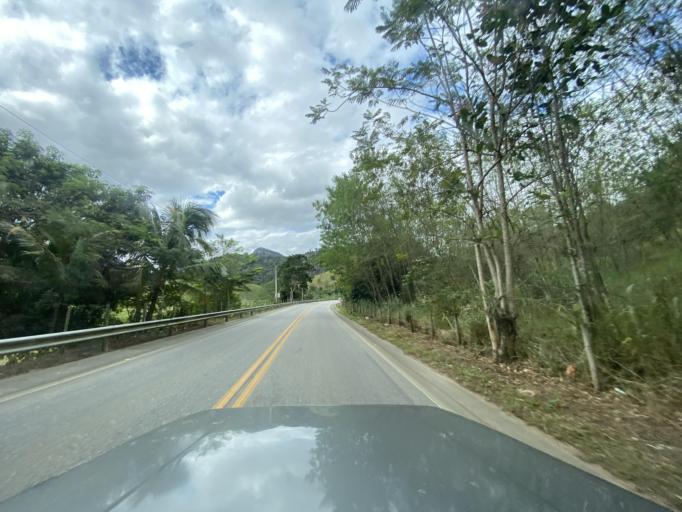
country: BR
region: Espirito Santo
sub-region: Jeronimo Monteiro
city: Jeronimo Monteiro
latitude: -20.7685
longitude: -41.4321
